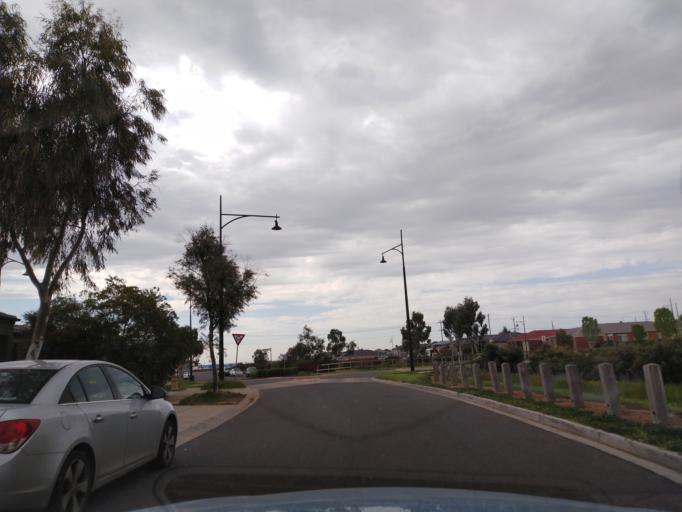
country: AU
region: Victoria
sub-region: Wyndham
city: Williams Landing
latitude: -37.8383
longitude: 144.7166
